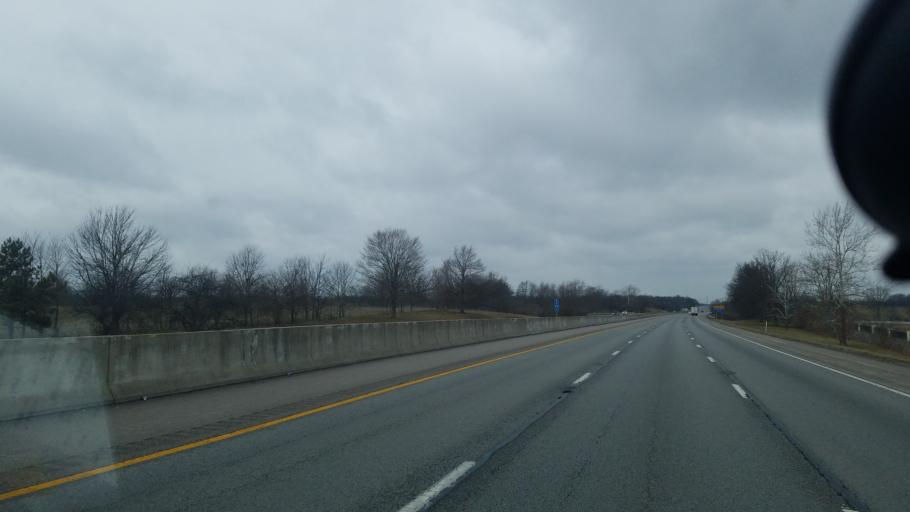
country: US
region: Kentucky
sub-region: Clark County
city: Winchester
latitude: 38.0374
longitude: -84.2912
